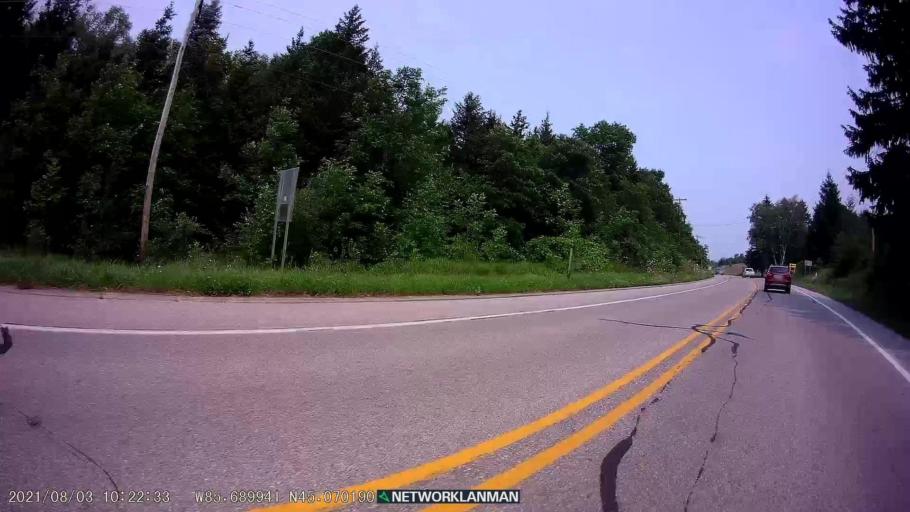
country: US
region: Michigan
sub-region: Leelanau County
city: Leland
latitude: 45.0703
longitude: -85.6898
